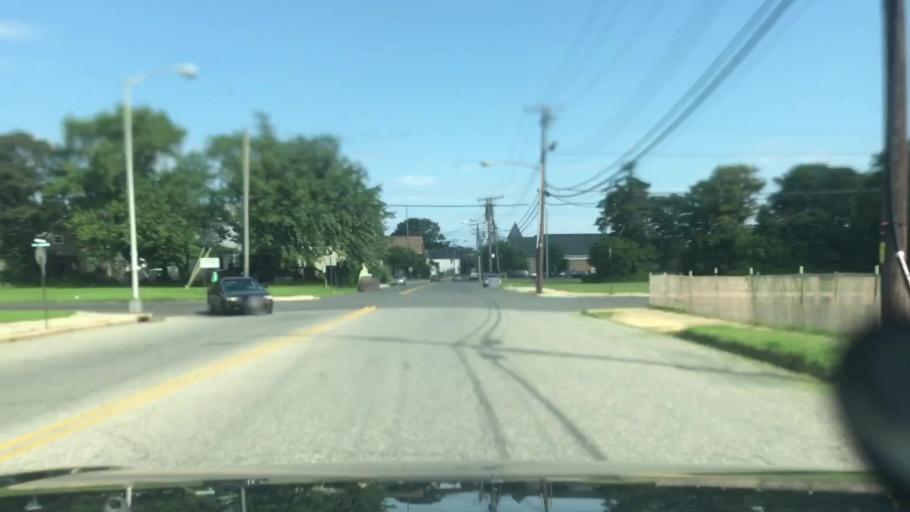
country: US
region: New Jersey
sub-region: Monmouth County
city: Long Branch
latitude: 40.3054
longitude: -73.9858
